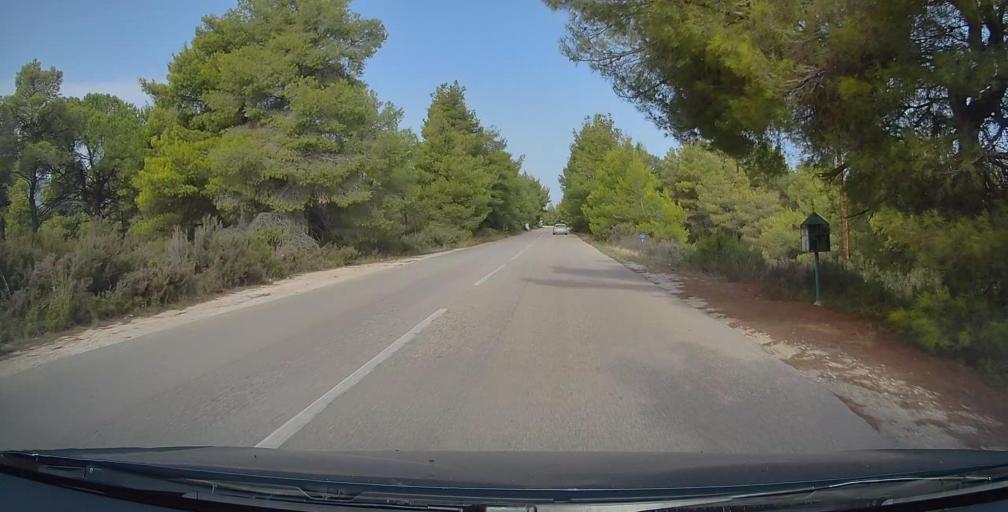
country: GR
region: Central Macedonia
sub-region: Nomos Chalkidikis
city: Sarti
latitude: 40.1242
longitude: 23.9664
